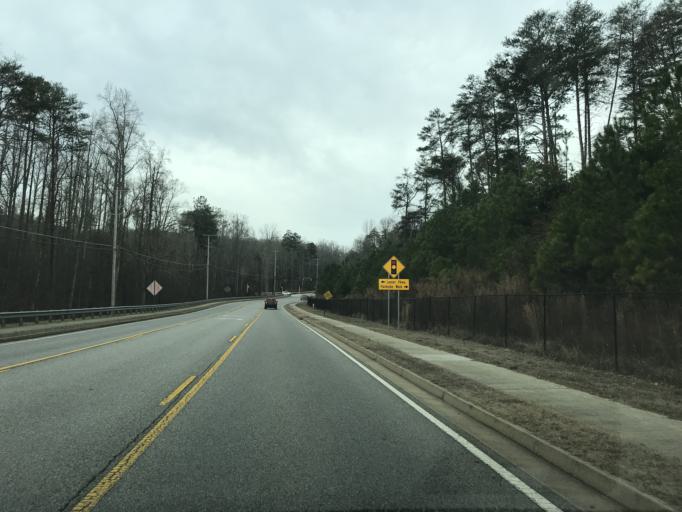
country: US
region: Georgia
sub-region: Forsyth County
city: Cumming
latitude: 34.2234
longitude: -84.1170
